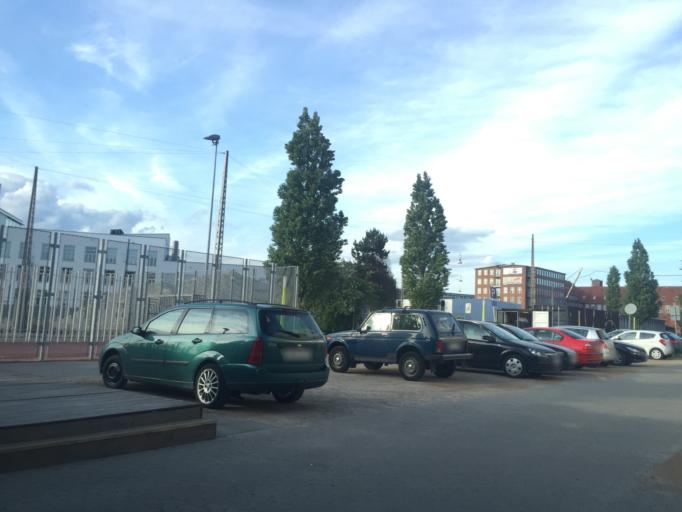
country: DK
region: Capital Region
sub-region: Kobenhavn
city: Christianshavn
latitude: 55.6668
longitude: 12.6104
